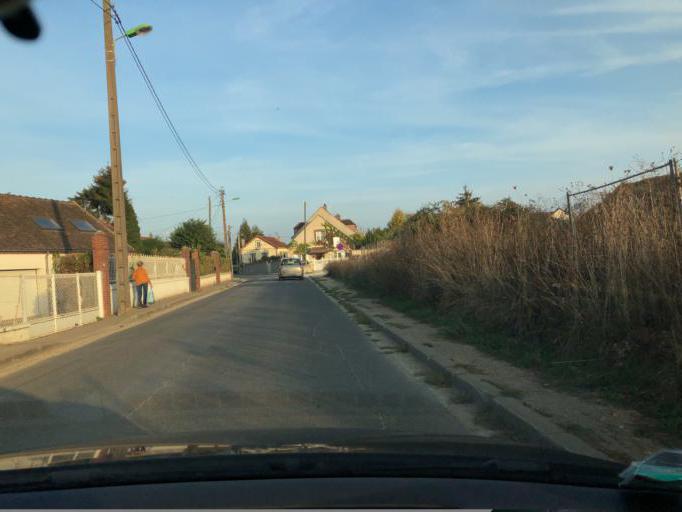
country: FR
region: Bourgogne
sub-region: Departement de l'Yonne
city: Saint-Clement
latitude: 48.2161
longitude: 3.2923
